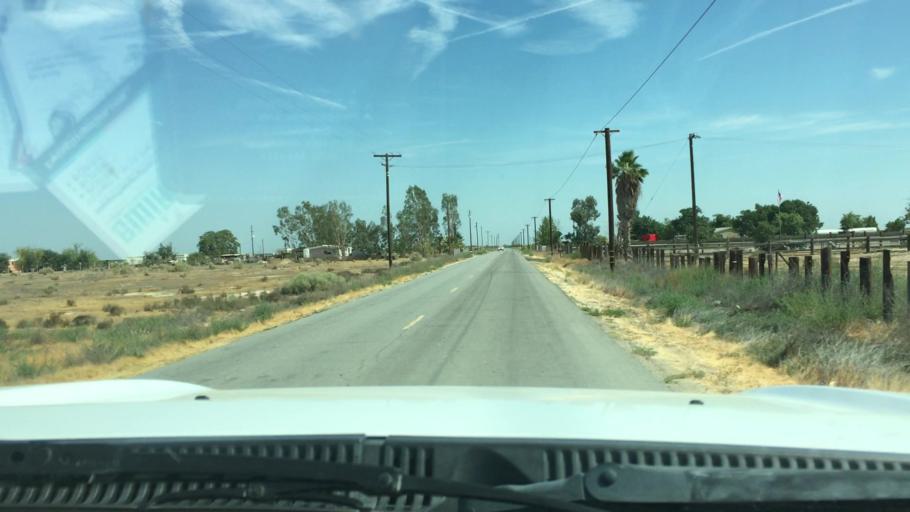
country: US
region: California
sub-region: Kern County
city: Buttonwillow
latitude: 35.4279
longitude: -119.3762
